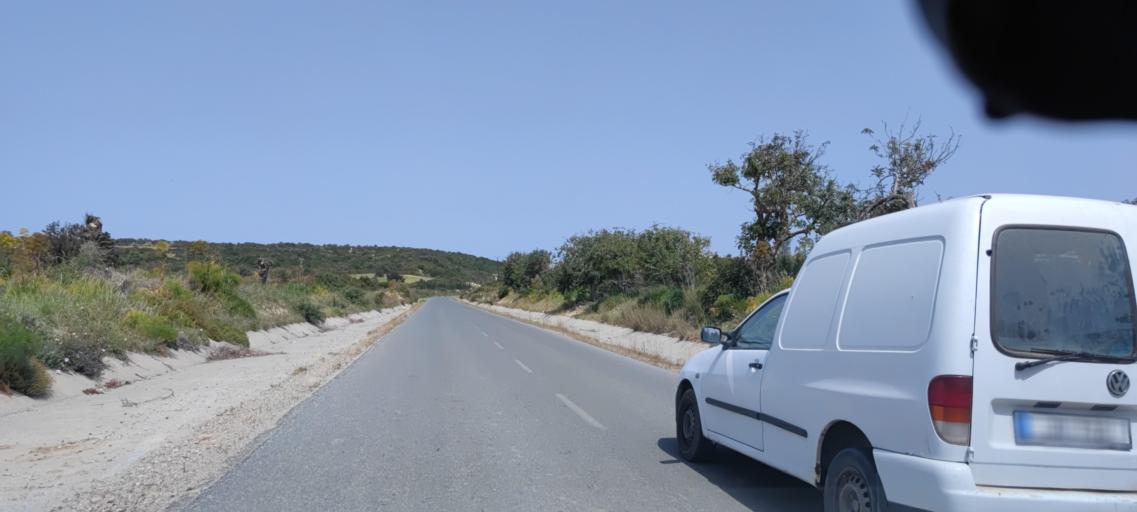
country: CY
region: Ammochostos
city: Rizokarpaso
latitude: 35.5842
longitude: 34.3963
